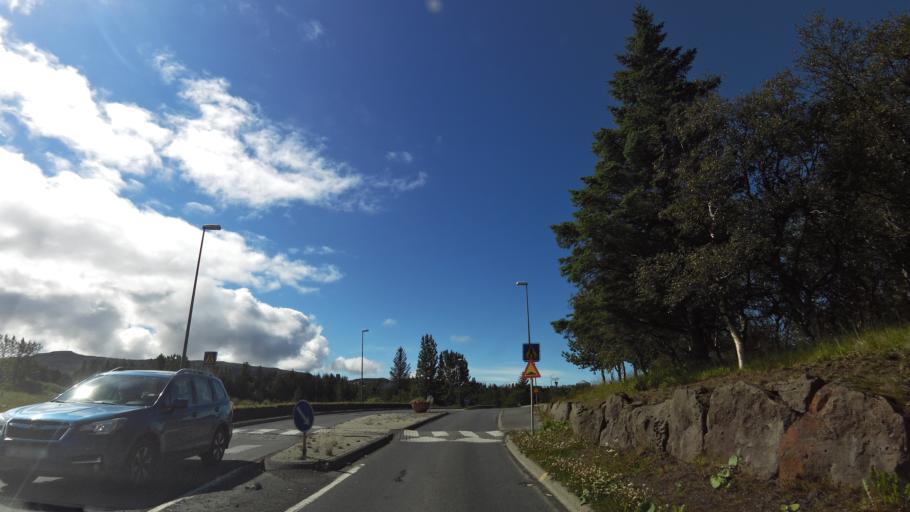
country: IS
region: Capital Region
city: Mosfellsbaer
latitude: 64.1673
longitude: -21.6791
